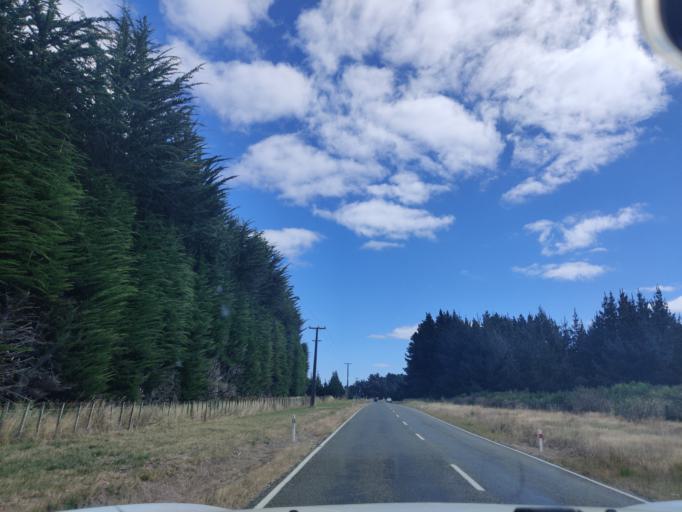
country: NZ
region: Manawatu-Wanganui
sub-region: Horowhenua District
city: Foxton
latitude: -40.3762
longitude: 175.2523
